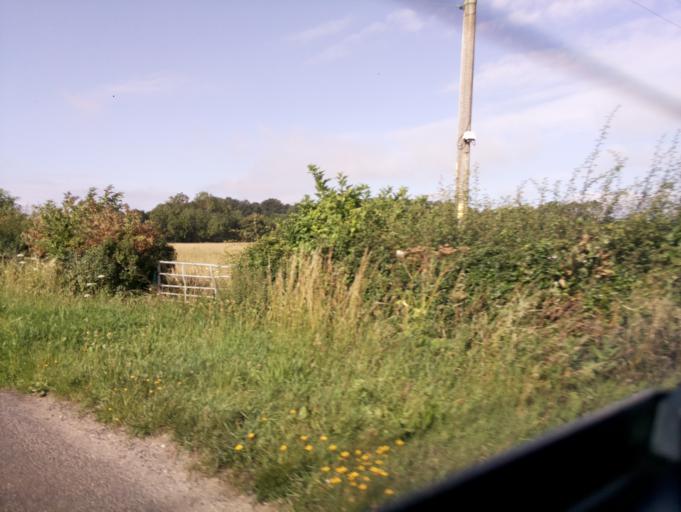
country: GB
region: England
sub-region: Oxfordshire
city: Faringdon
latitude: 51.6513
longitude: -1.6056
